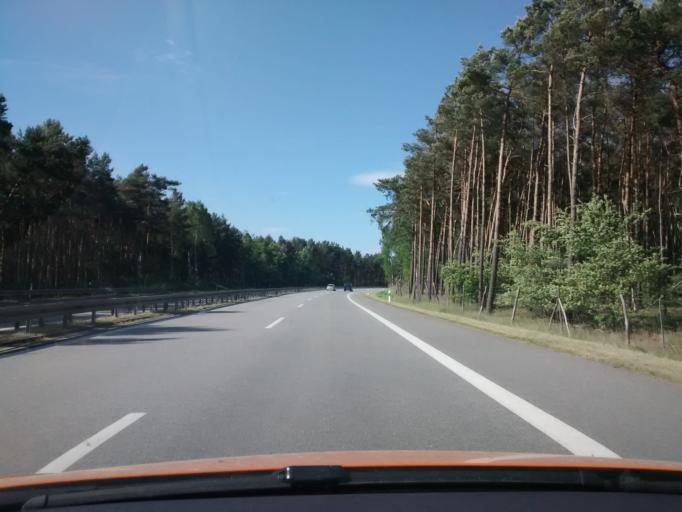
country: DE
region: Brandenburg
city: Trebbin
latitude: 52.1928
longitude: 13.2540
